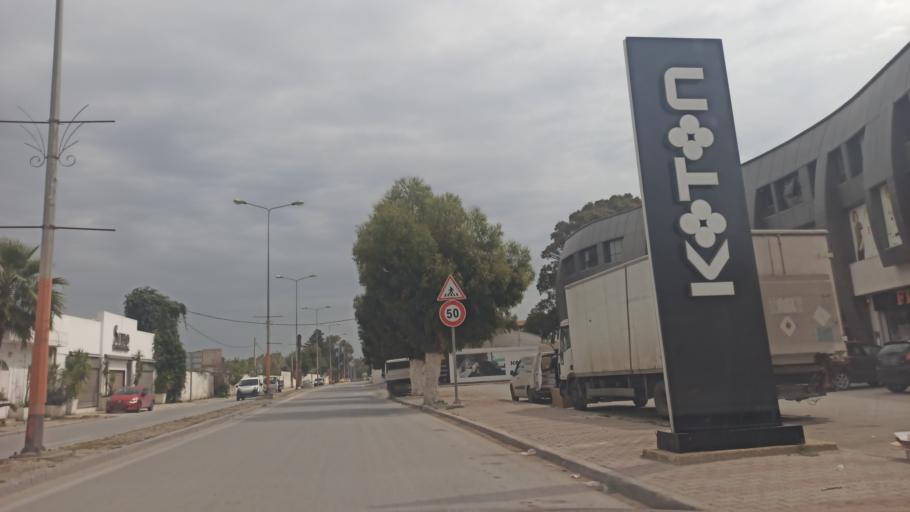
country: TN
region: Ariana
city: Ariana
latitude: 36.8757
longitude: 10.2461
